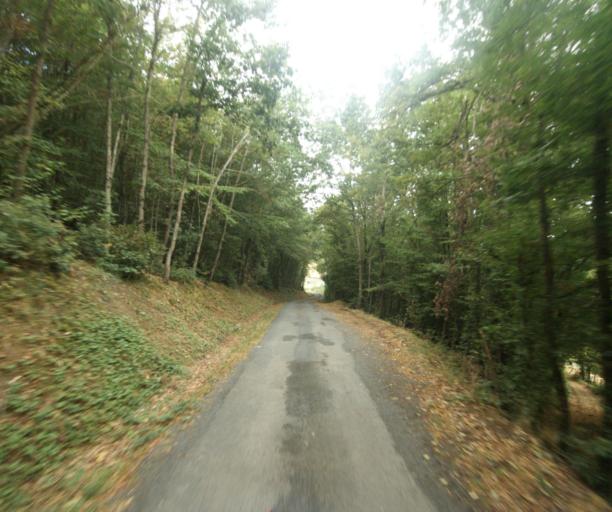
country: FR
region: Rhone-Alpes
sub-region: Departement du Rhone
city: Bessenay
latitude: 45.7873
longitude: 4.5229
